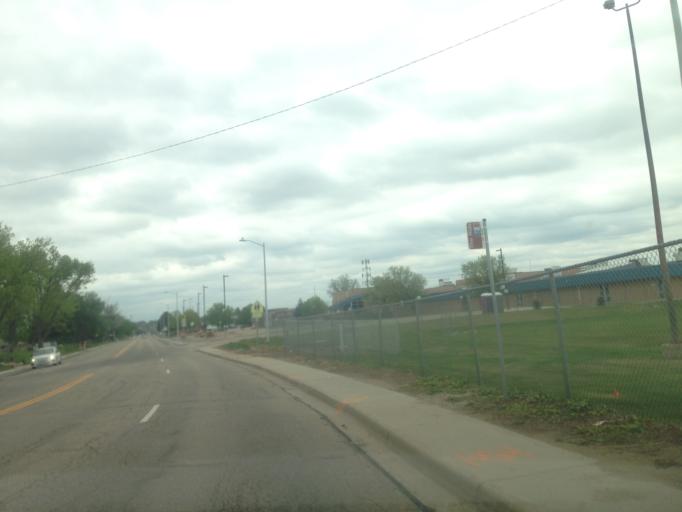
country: US
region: Colorado
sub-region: Boulder County
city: Longmont
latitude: 40.1428
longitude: -105.1215
